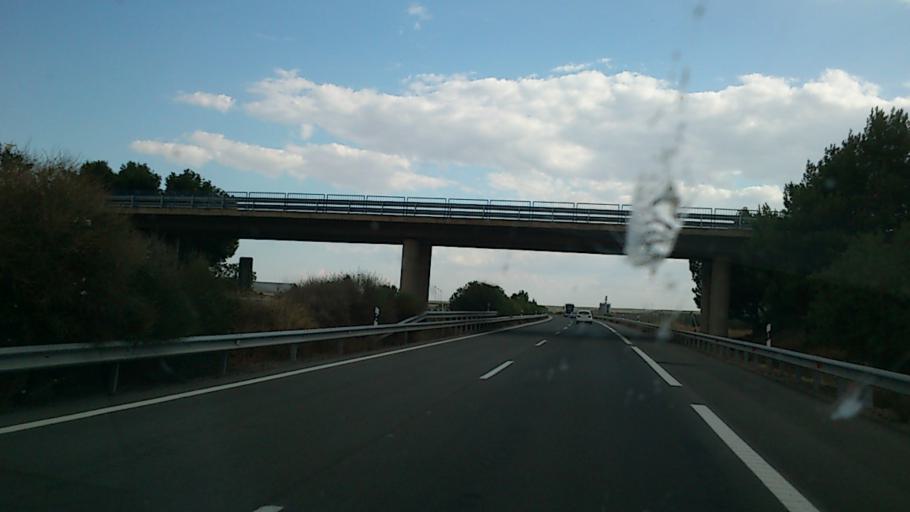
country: ES
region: La Rioja
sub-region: Provincia de La Rioja
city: Aldeanueva de Ebro
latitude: 42.2259
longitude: -1.8985
